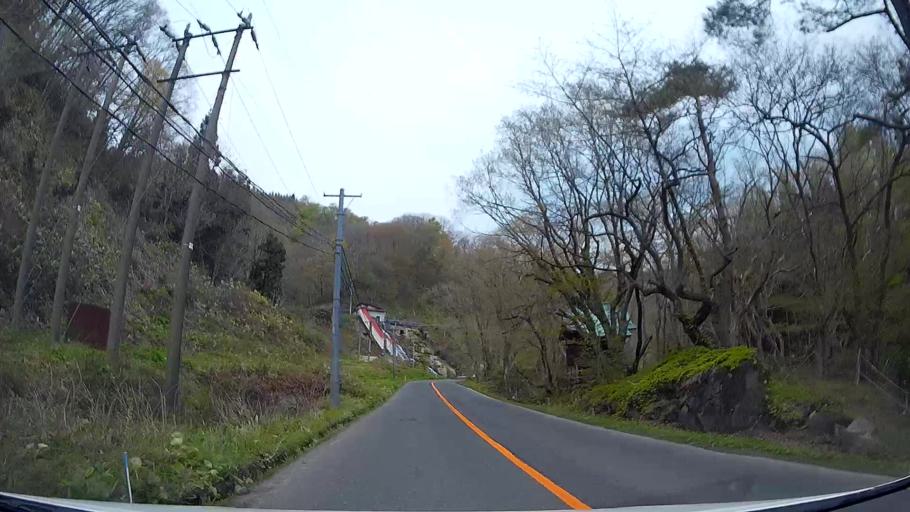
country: JP
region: Akita
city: Hanawa
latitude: 40.3733
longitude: 140.8794
